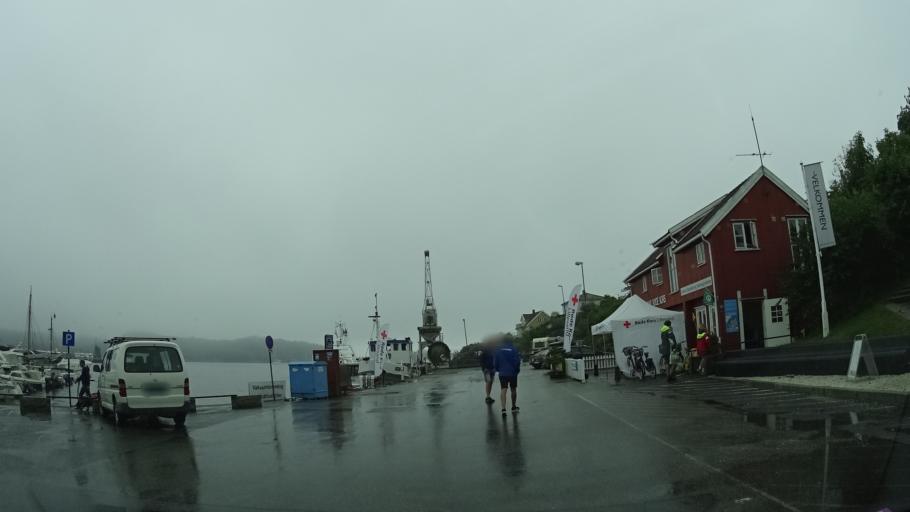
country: NO
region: Aust-Agder
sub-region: Lillesand
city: Lillesand
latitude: 58.2470
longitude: 8.3781
